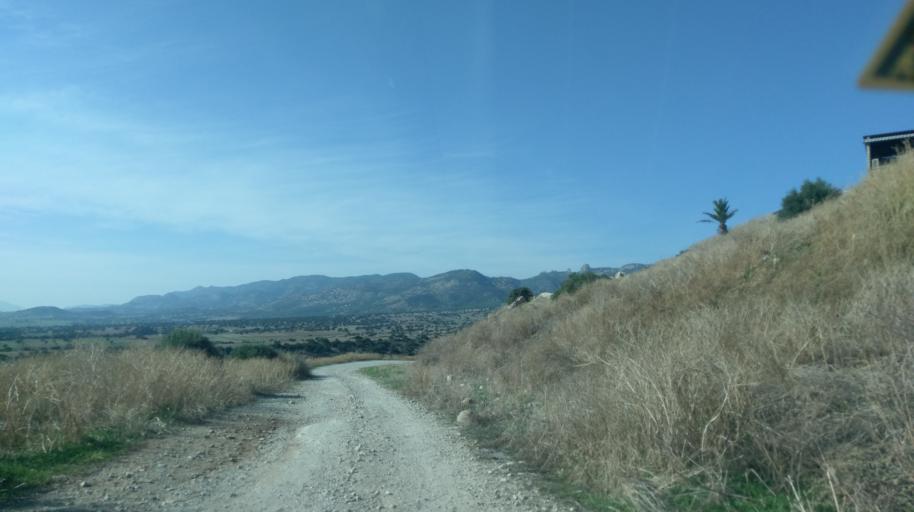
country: CY
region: Ammochostos
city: Trikomo
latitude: 35.3371
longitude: 33.8694
